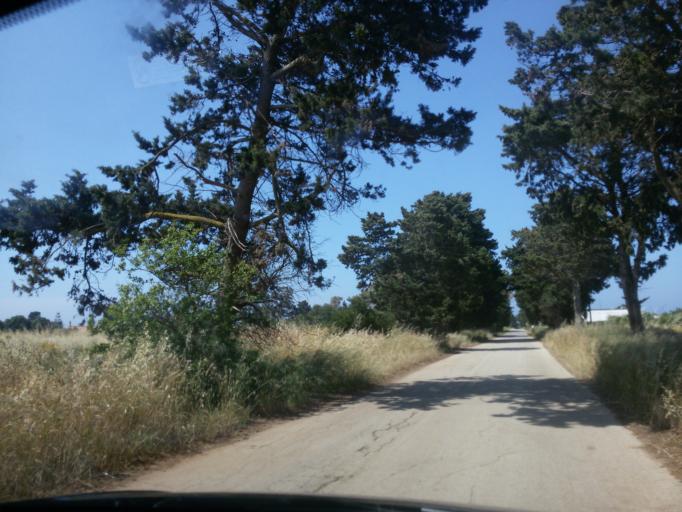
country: IT
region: Apulia
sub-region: Provincia di Brindisi
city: Brindisi
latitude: 40.6630
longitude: 17.8608
